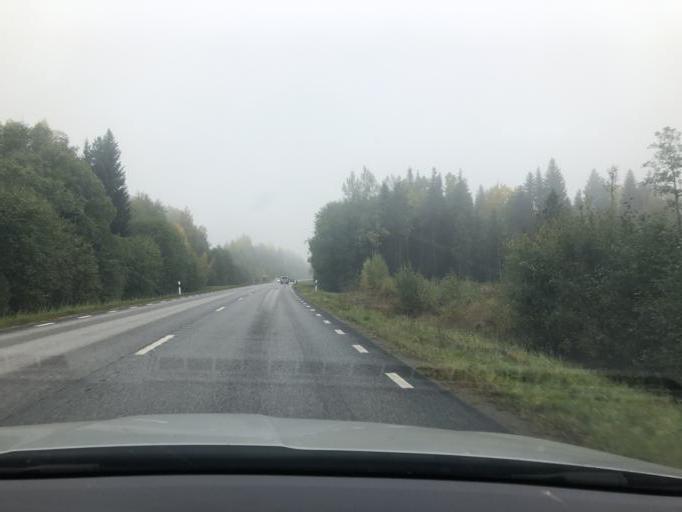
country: SE
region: Uppsala
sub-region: Tierps Kommun
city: Tierp
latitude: 60.3168
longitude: 17.5375
